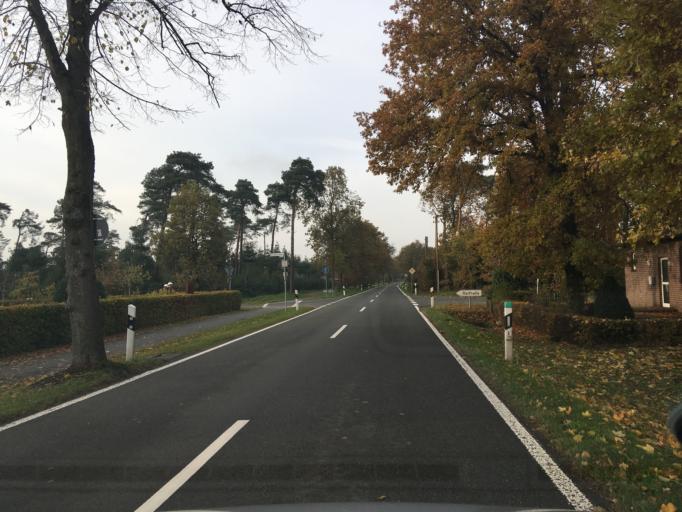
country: DE
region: North Rhine-Westphalia
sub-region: Regierungsbezirk Munster
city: Velen
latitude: 51.9182
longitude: 6.9610
